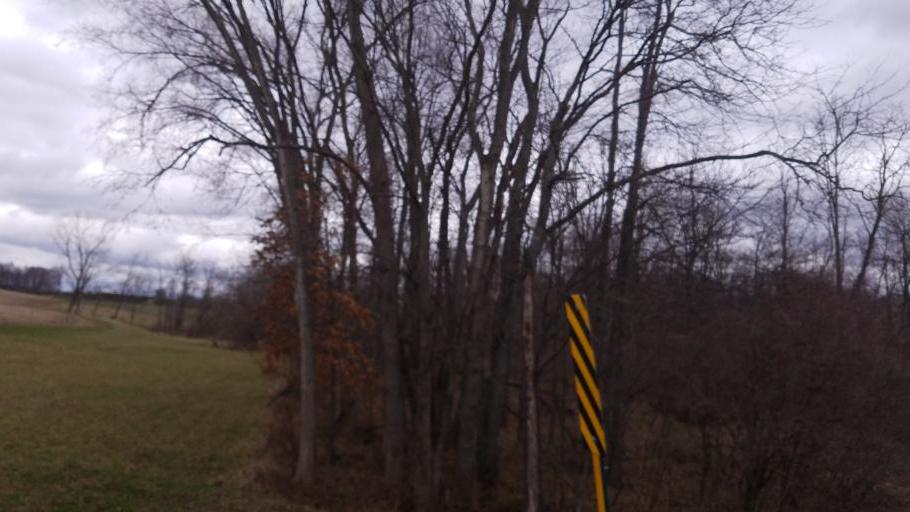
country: US
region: Ohio
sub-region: Licking County
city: Utica
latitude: 40.1923
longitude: -82.3709
